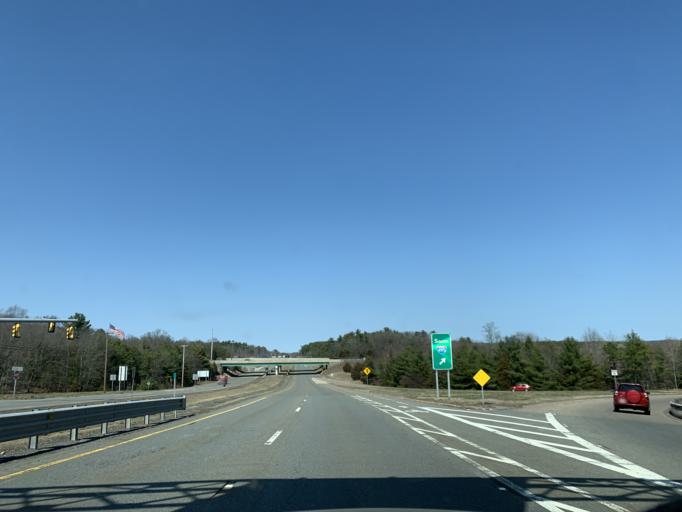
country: US
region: Massachusetts
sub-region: Norfolk County
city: Wrentham
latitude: 42.0347
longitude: -71.3078
